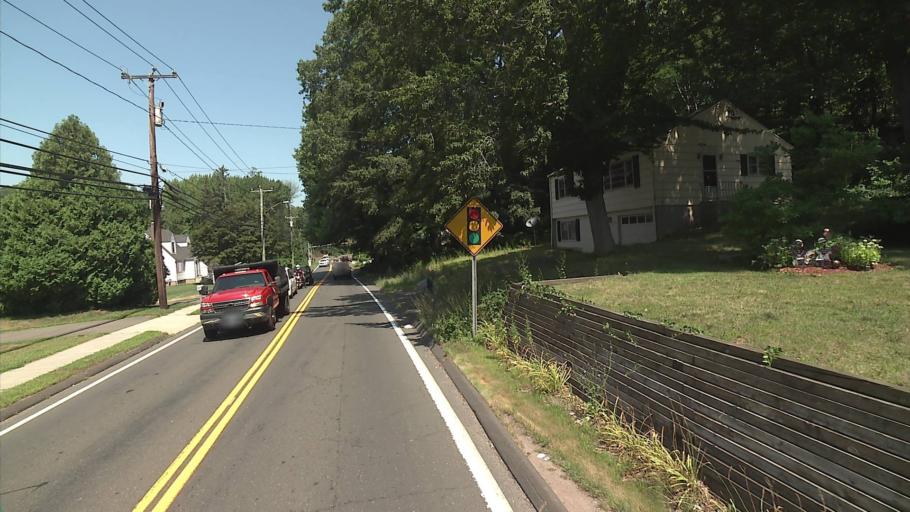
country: US
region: Connecticut
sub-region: New Haven County
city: Branford Center
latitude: 41.2668
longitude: -72.8310
